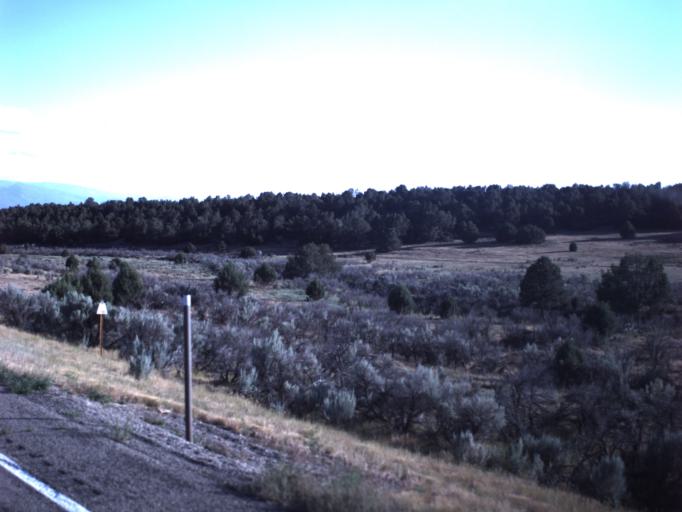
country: US
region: Utah
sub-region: Sanpete County
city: Fairview
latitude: 39.6657
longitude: -111.4532
